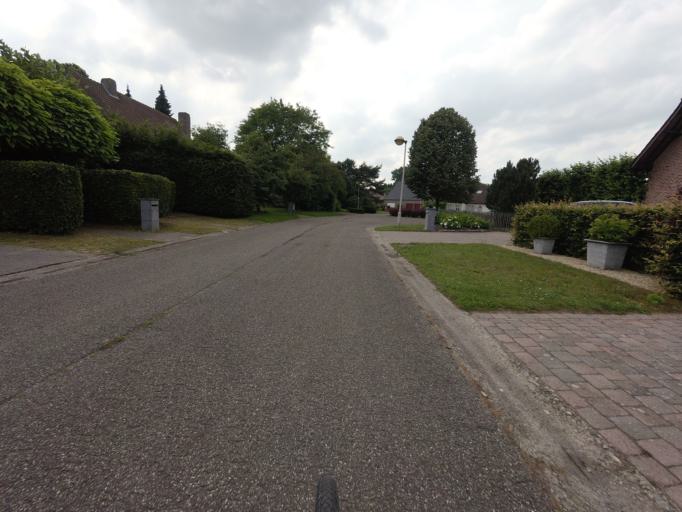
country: BE
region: Flanders
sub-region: Provincie Antwerpen
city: Schilde
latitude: 51.2181
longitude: 4.5832
